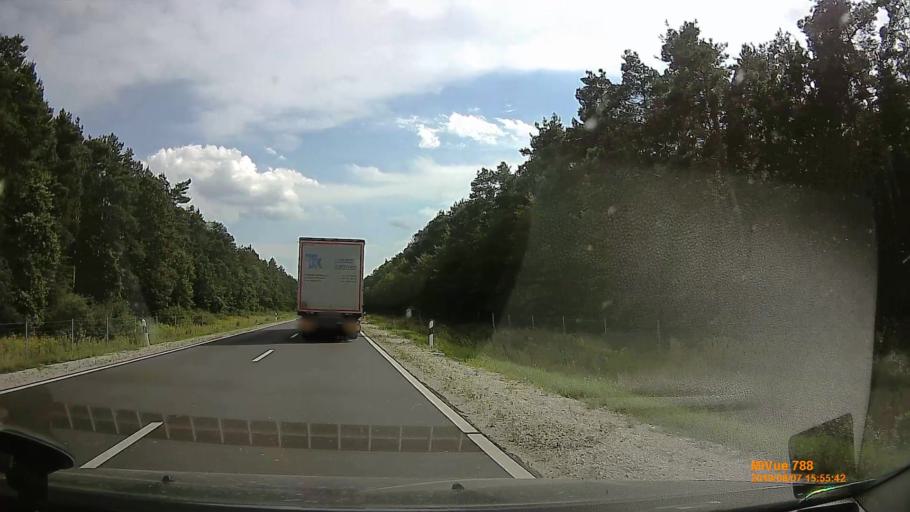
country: HU
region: Vas
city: Kormend
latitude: 47.0707
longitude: 16.6174
